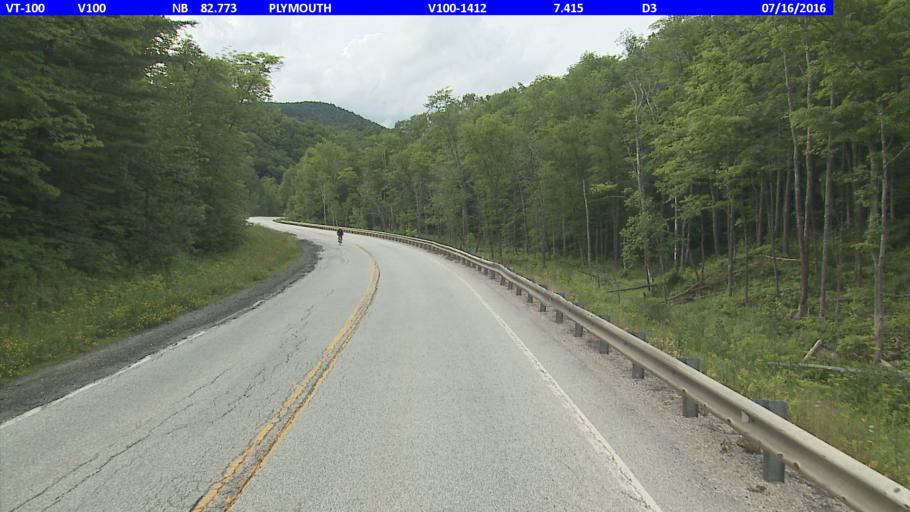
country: US
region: Vermont
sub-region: Rutland County
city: Rutland
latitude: 43.5564
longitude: -72.7572
